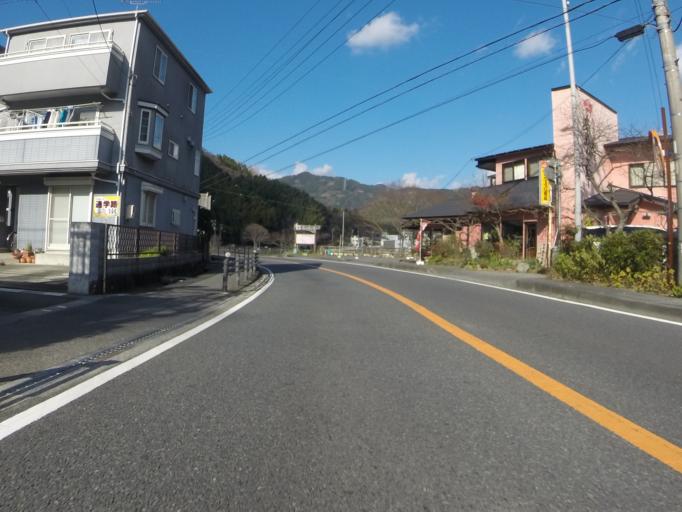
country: JP
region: Shizuoka
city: Fujinomiya
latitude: 35.0925
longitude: 138.5158
